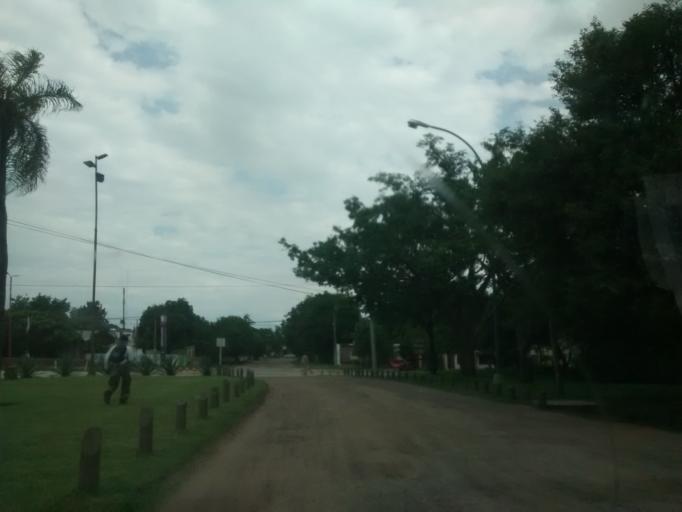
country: AR
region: Chaco
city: Resistencia
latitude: -27.4379
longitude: -58.9814
